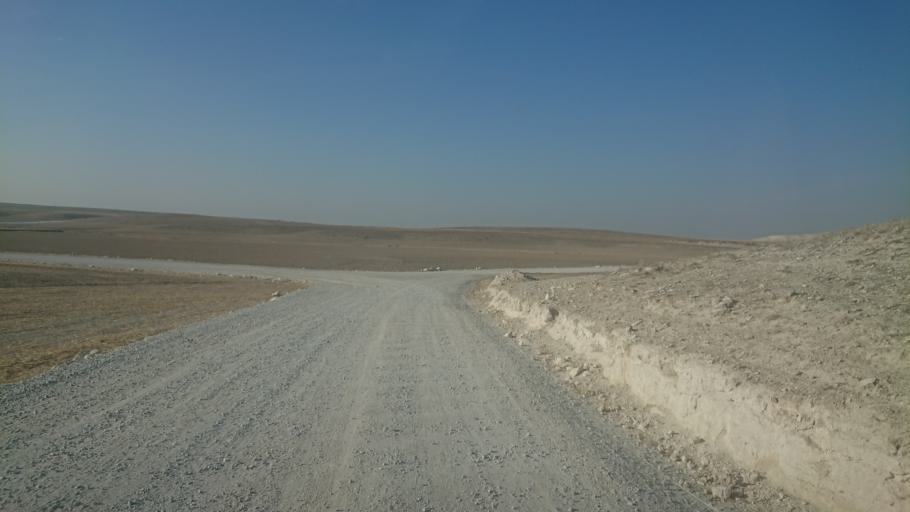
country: TR
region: Aksaray
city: Sultanhani
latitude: 38.0830
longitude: 33.6213
